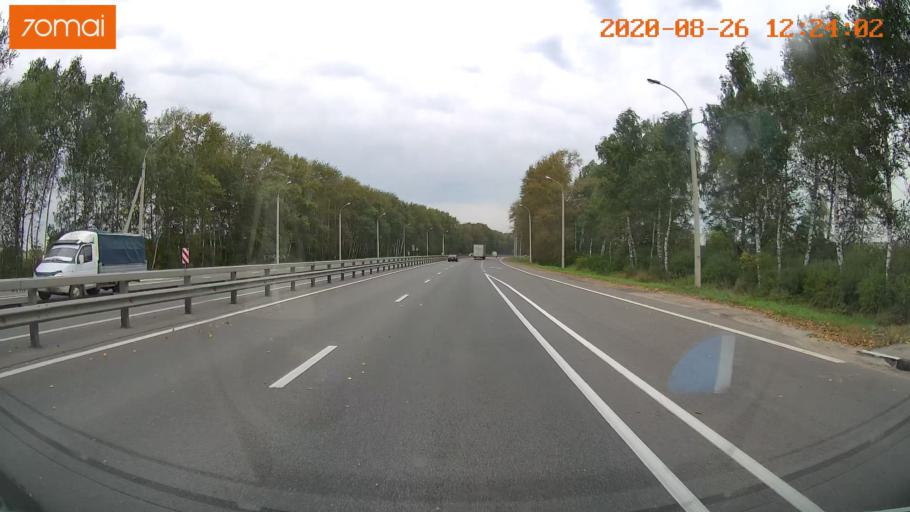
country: RU
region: Rjazan
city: Murmino
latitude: 54.5095
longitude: 39.8996
